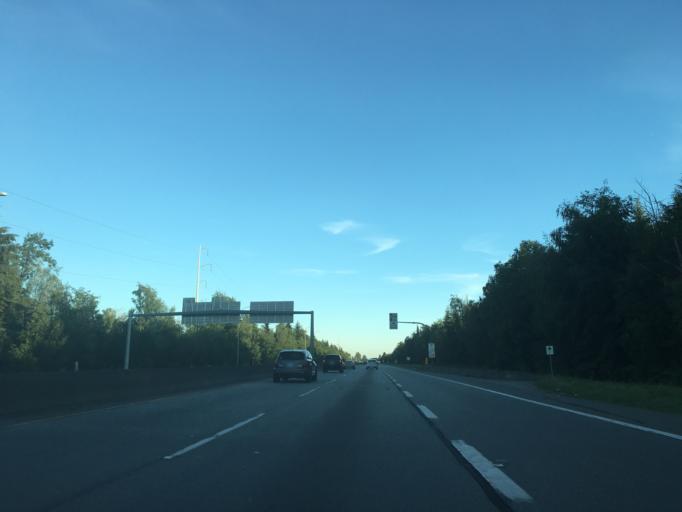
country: CA
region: British Columbia
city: Richmond
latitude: 49.1645
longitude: -123.0868
